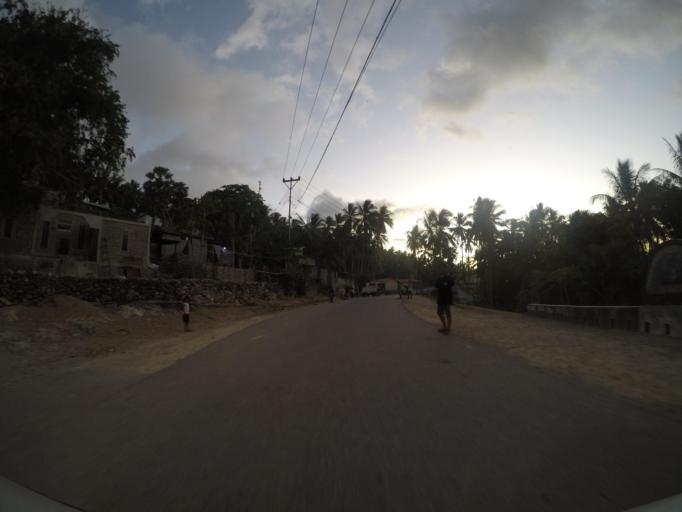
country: TL
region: Lautem
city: Lospalos
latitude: -8.3692
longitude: 127.0383
